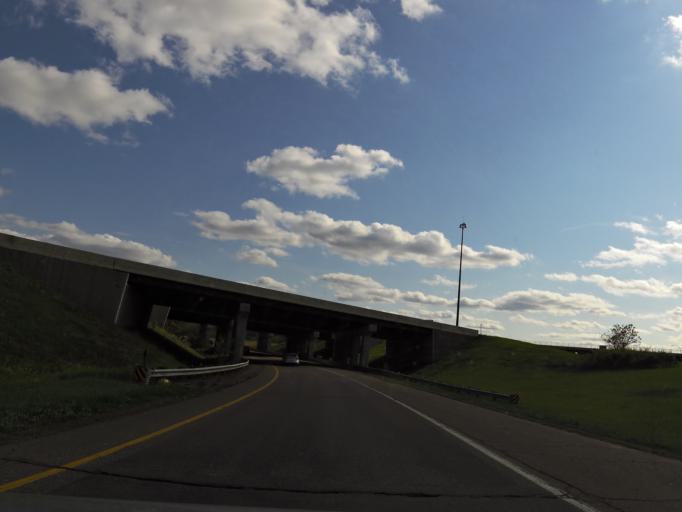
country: US
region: Minnesota
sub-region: Dakota County
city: Mendota Heights
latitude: 44.8634
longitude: -93.1478
